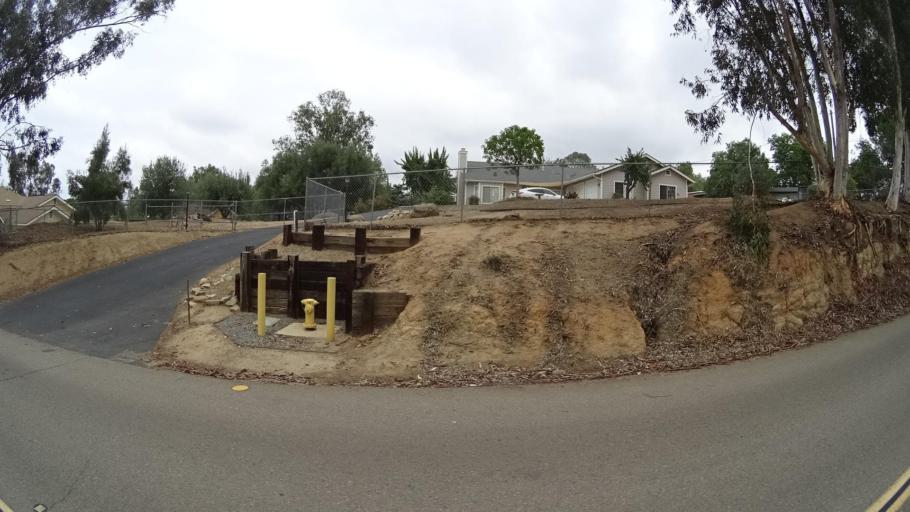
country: US
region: California
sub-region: San Diego County
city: Ramona
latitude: 33.0357
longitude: -116.8615
